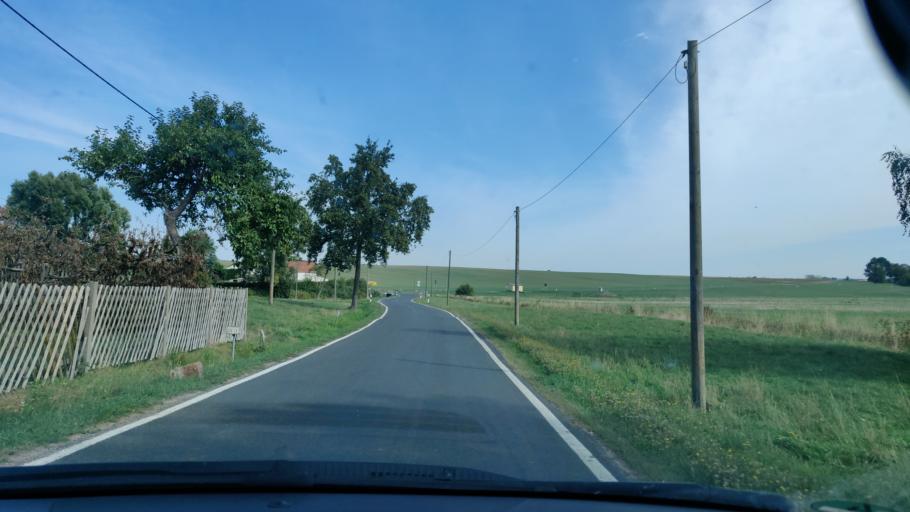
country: DE
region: Saxony
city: Konigsfeld
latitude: 51.0884
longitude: 12.7589
